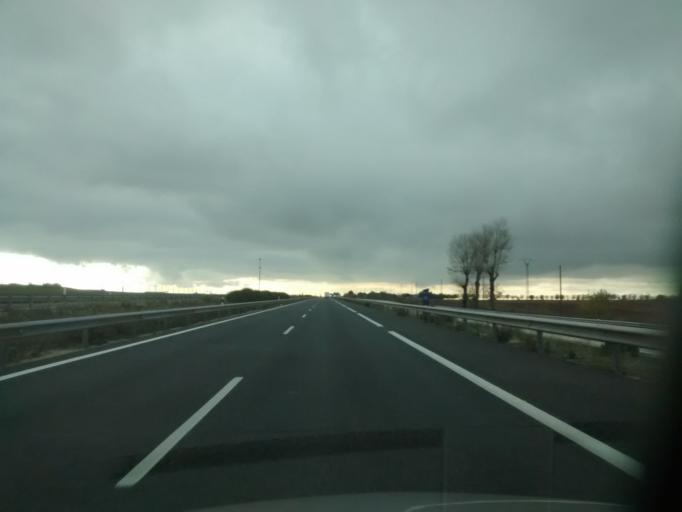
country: ES
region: Castille-La Mancha
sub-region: Provincia de Guadalajara
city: Trijueque
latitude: 40.7885
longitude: -2.9733
